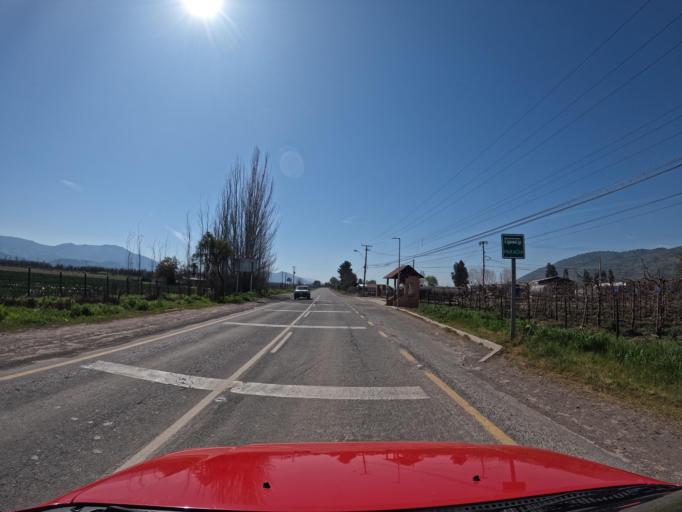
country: CL
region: Maule
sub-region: Provincia de Curico
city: Rauco
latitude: -35.0207
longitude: -71.4287
